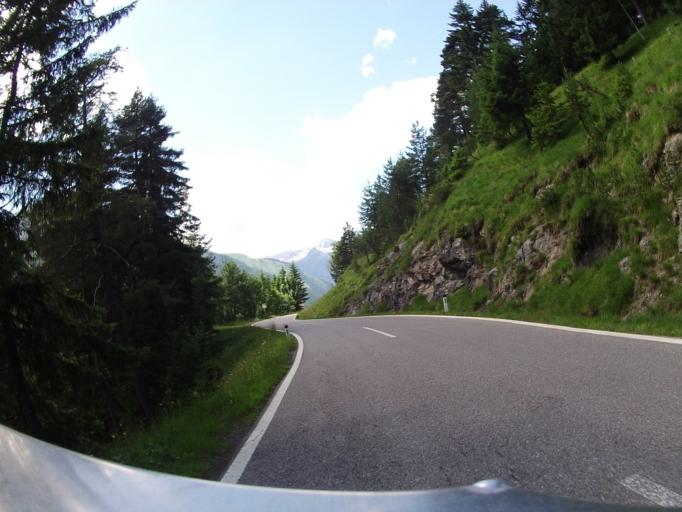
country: AT
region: Tyrol
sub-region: Politischer Bezirk Reutte
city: Elmen
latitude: 47.3044
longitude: 10.5943
